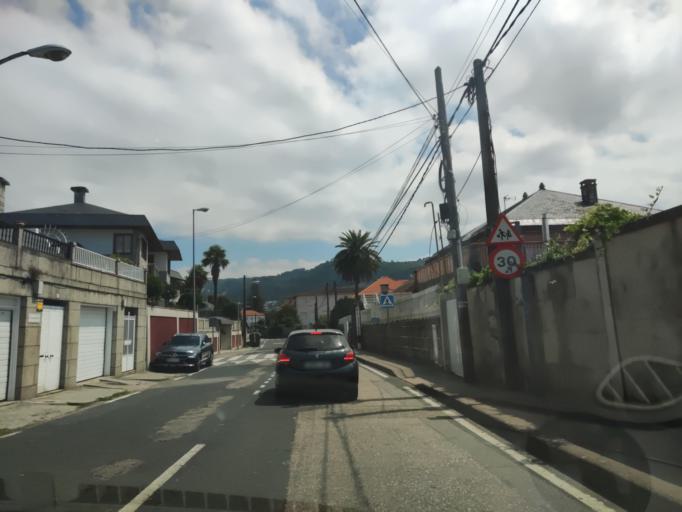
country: ES
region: Galicia
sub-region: Provincia de Pontevedra
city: Vigo
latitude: 42.2538
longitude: -8.7008
